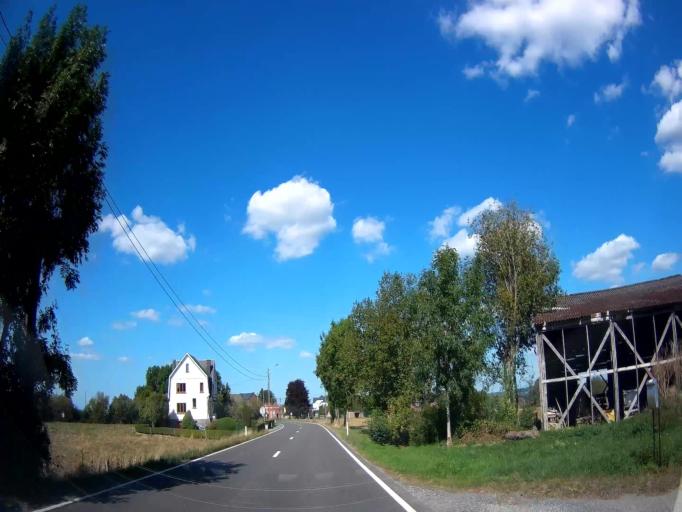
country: BE
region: Wallonia
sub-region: Province de Namur
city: Houyet
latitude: 50.1984
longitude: 4.9434
